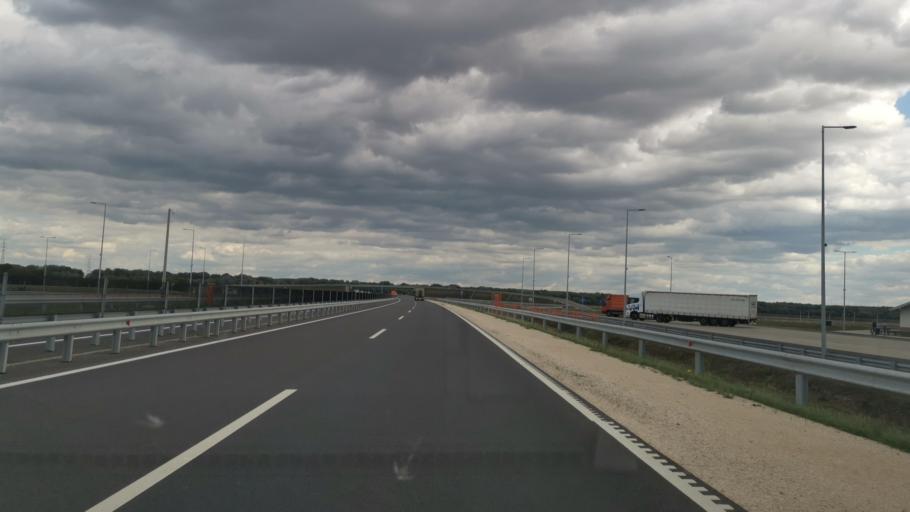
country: HU
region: Jasz-Nagykun-Szolnok
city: Szajol
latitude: 47.2134
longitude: 20.2693
